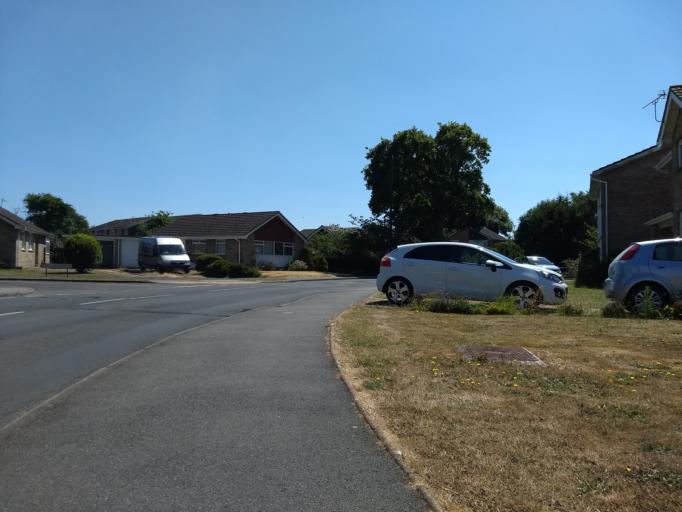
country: GB
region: England
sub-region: Isle of Wight
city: Gurnard
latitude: 50.7599
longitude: -1.3110
